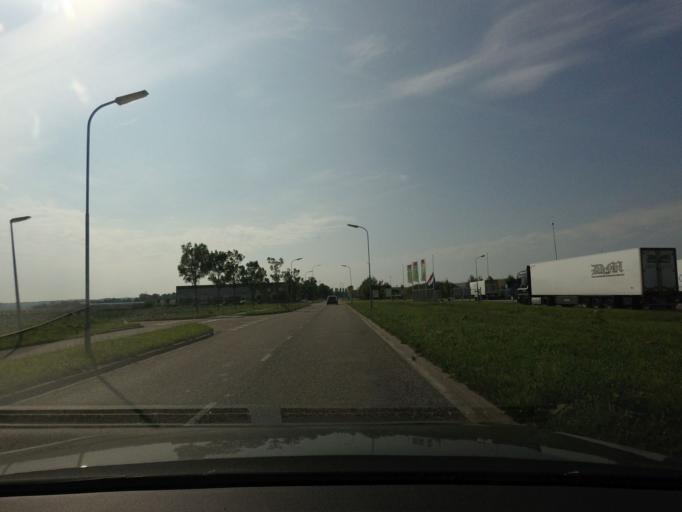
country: NL
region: North Holland
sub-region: Gemeente Schagen
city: Harenkarspel
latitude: 52.7149
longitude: 4.7367
